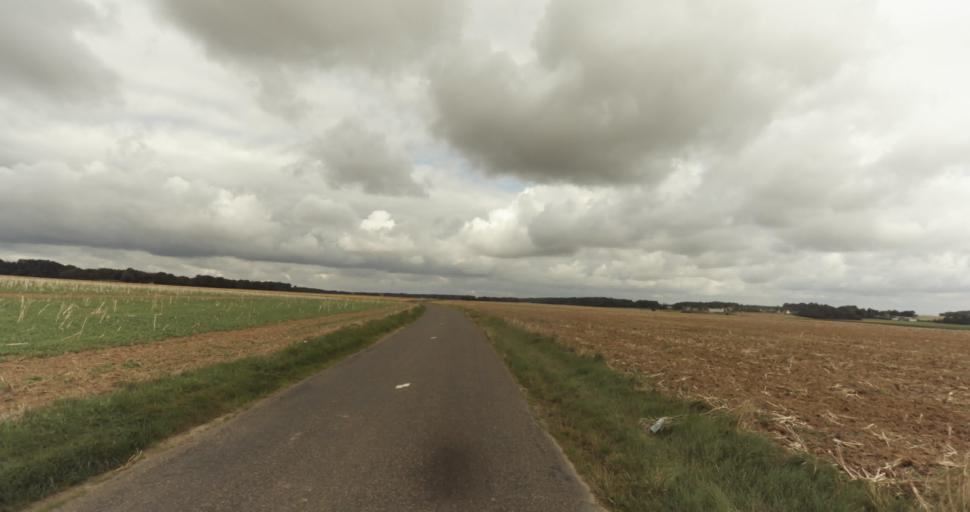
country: FR
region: Haute-Normandie
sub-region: Departement de l'Eure
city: Menilles
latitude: 48.9654
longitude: 1.2877
